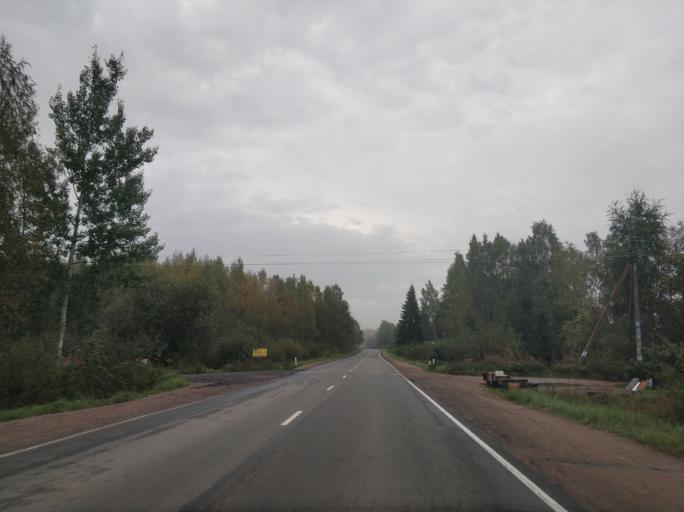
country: RU
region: Leningrad
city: Shcheglovo
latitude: 60.0963
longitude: 30.8456
